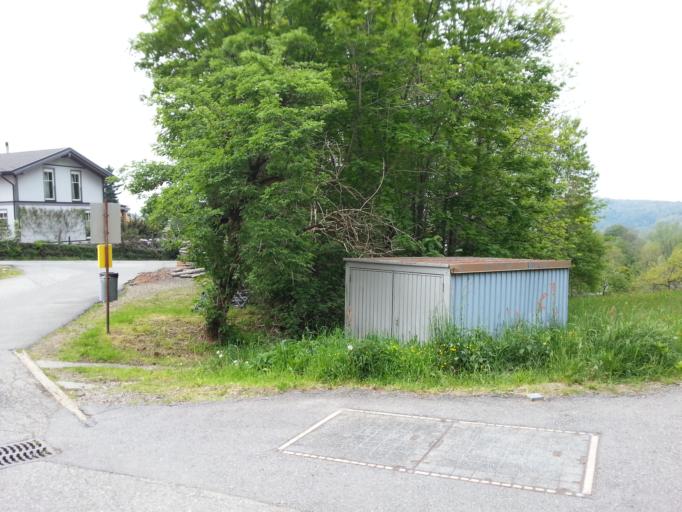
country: CH
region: Ticino
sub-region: Lugano District
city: Bioggio
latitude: 46.0361
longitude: 8.8717
